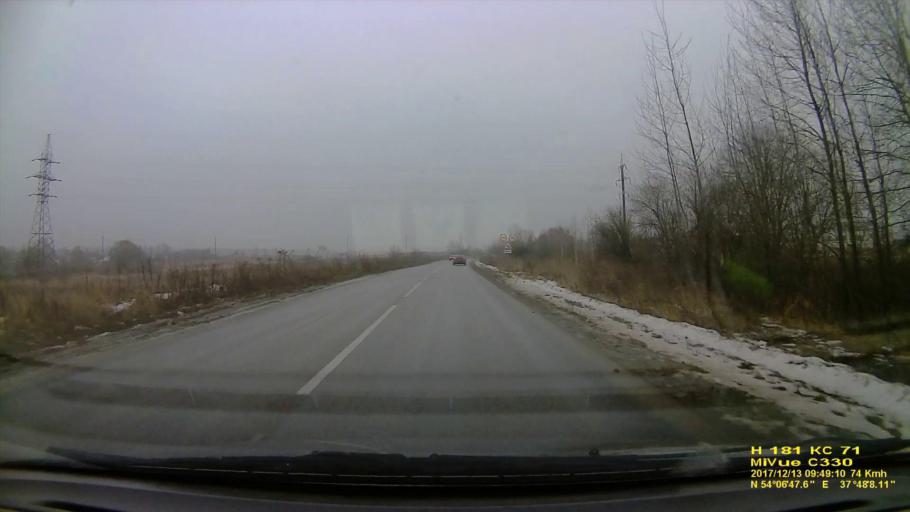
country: RU
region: Tula
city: Bolokhovo
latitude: 54.1132
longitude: 37.8022
